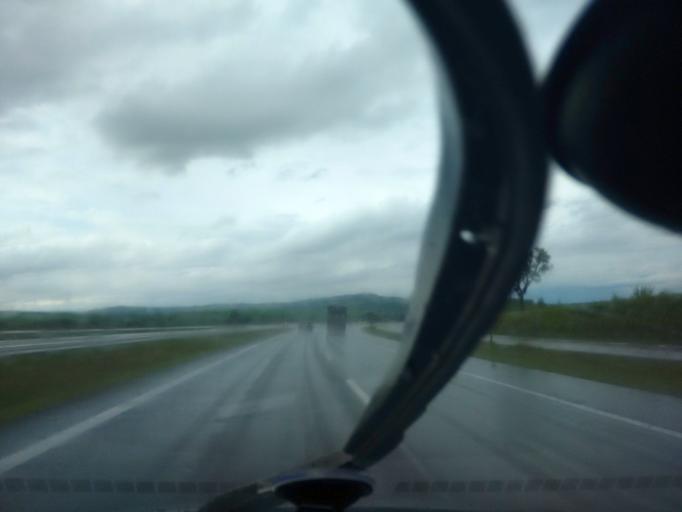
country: BR
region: Sao Paulo
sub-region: Iracemapolis
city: Iracemapolis
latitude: -22.5823
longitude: -47.4590
